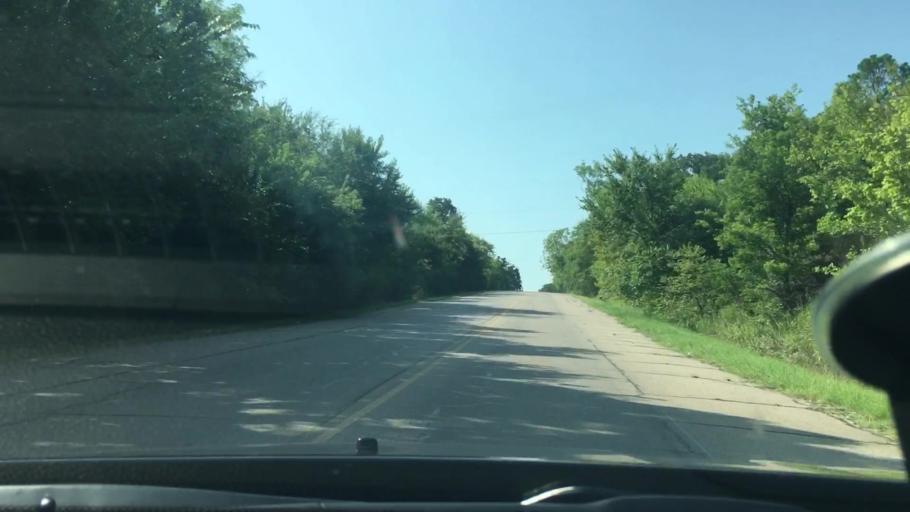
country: US
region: Oklahoma
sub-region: Bryan County
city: Durant
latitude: 34.0146
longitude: -96.3905
